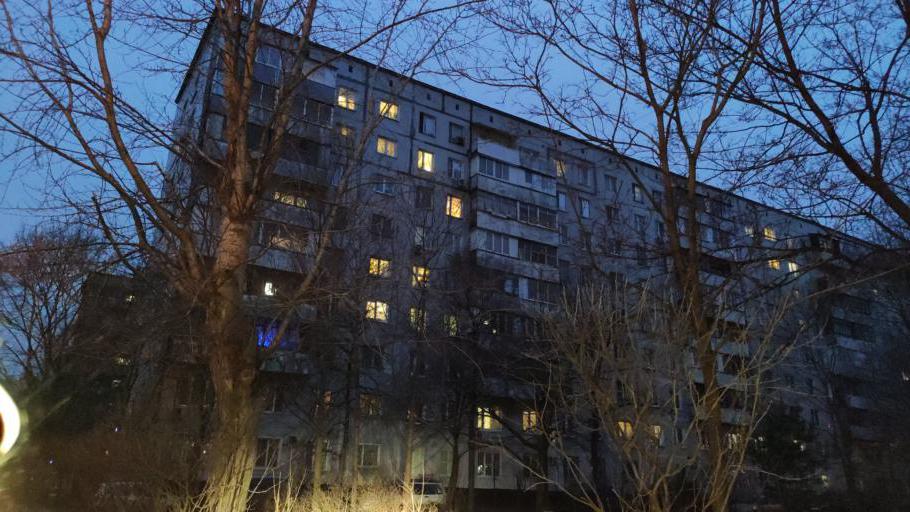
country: RU
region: Moscow
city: Lyublino
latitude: 55.6807
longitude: 37.7711
